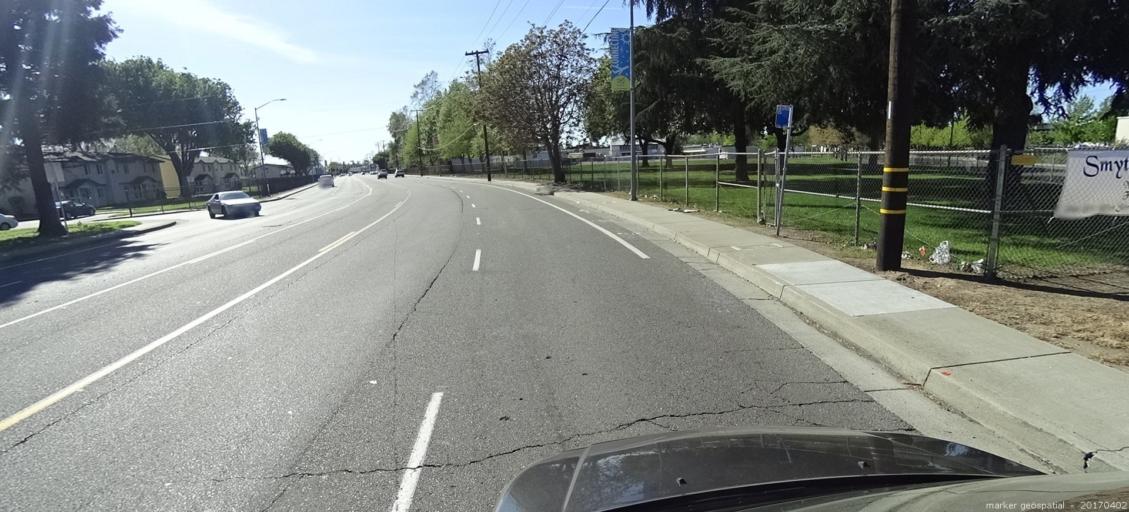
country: US
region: California
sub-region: Sacramento County
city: Sacramento
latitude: 38.5955
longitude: -121.4805
